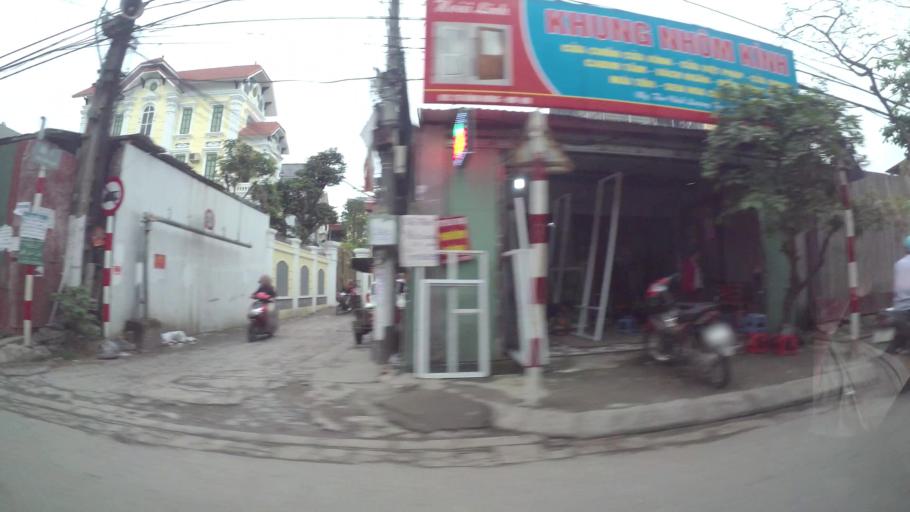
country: VN
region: Ha Noi
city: Hai BaTrung
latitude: 20.9862
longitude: 105.8762
